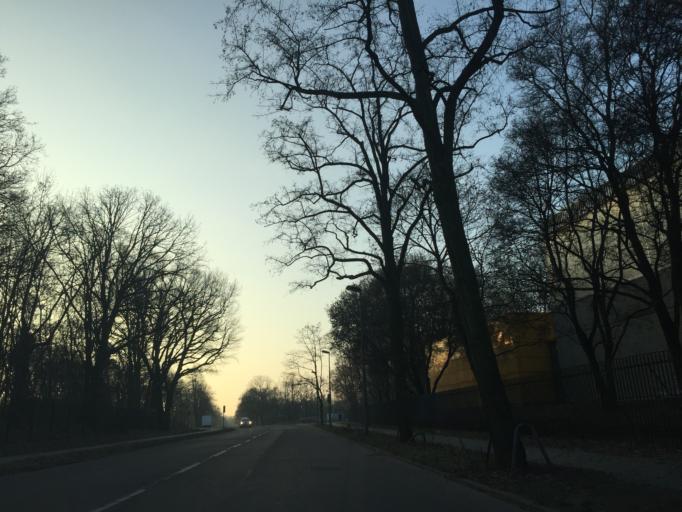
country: DE
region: Berlin
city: Haselhorst
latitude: 52.5126
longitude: 13.2307
